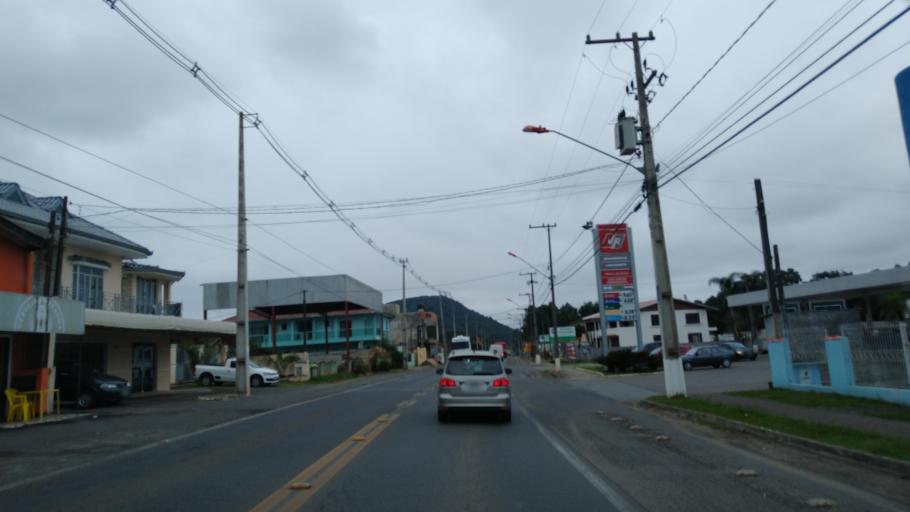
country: BR
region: Santa Catarina
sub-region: Porto Uniao
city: Porto Uniao
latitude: -26.2627
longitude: -51.0635
